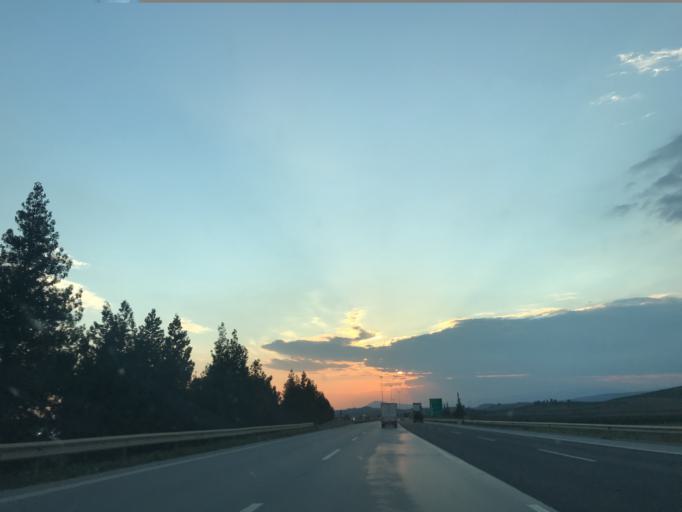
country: TR
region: Mersin
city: Yenice
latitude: 37.0111
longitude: 34.9870
